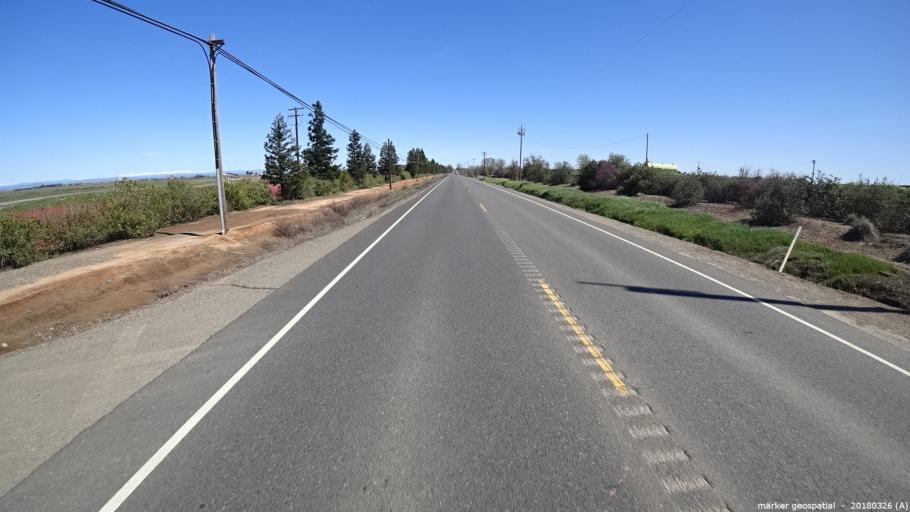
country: US
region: California
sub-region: Sacramento County
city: Rosemont
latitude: 38.5259
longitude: -121.3233
